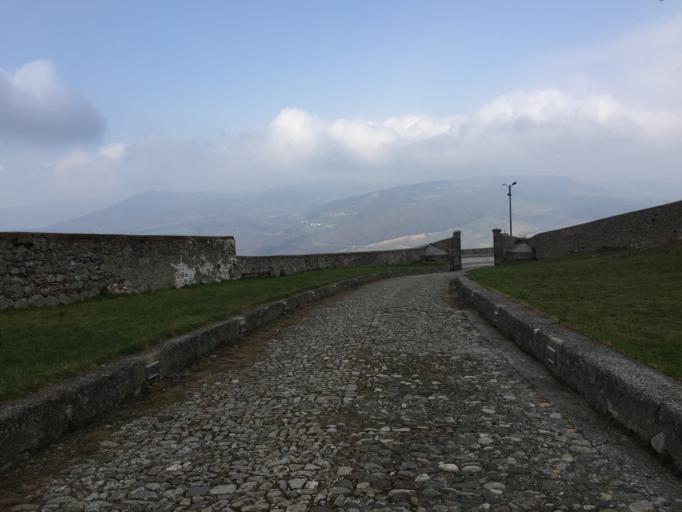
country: IT
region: Apulia
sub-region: Provincia di Foggia
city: Bovino
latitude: 41.2516
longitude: 15.3387
